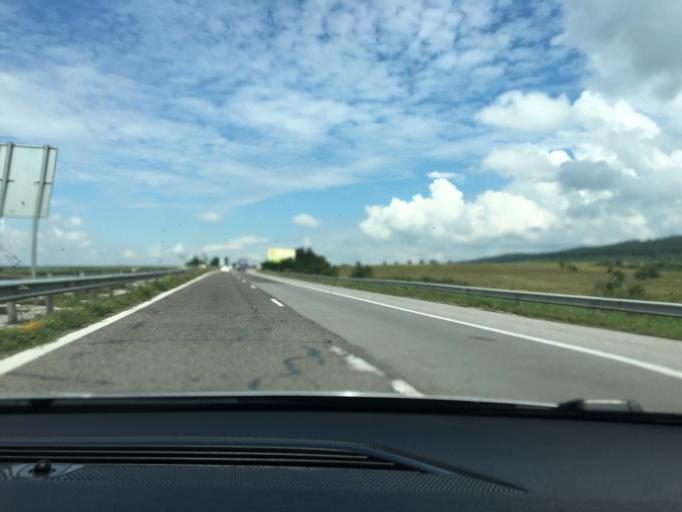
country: BG
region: Sofiya
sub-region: Obshtina Ikhtiman
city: Ikhtiman
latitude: 42.4088
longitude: 23.8646
